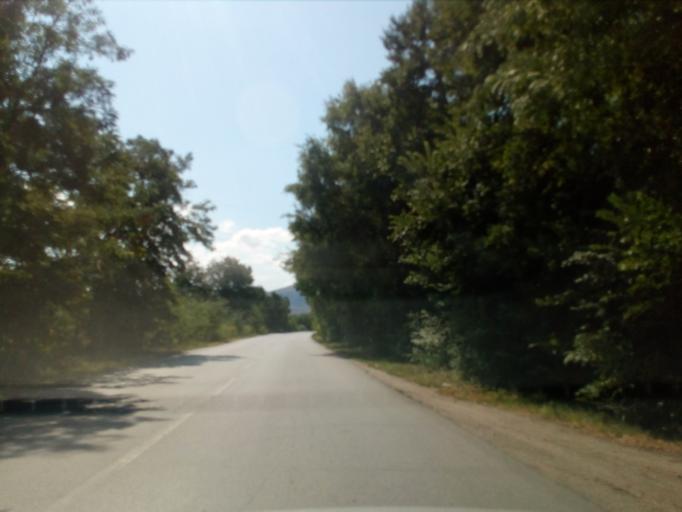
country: MK
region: Veles
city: Veles
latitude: 41.7365
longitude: 21.7605
